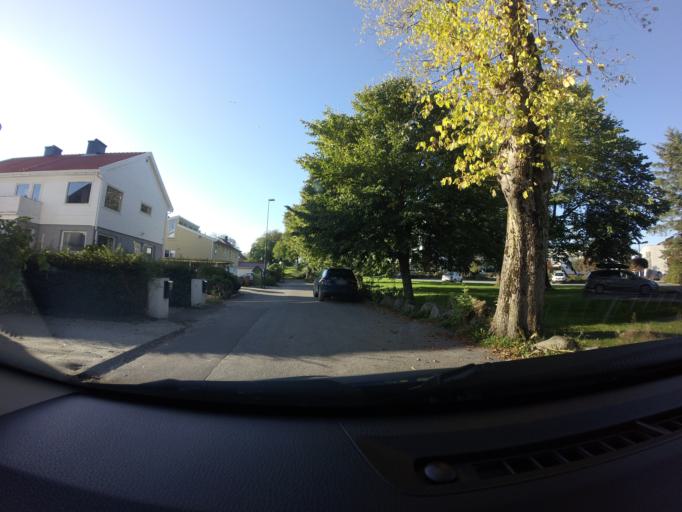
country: NO
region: Rogaland
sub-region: Stavanger
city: Stavanger
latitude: 58.9511
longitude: 5.7337
